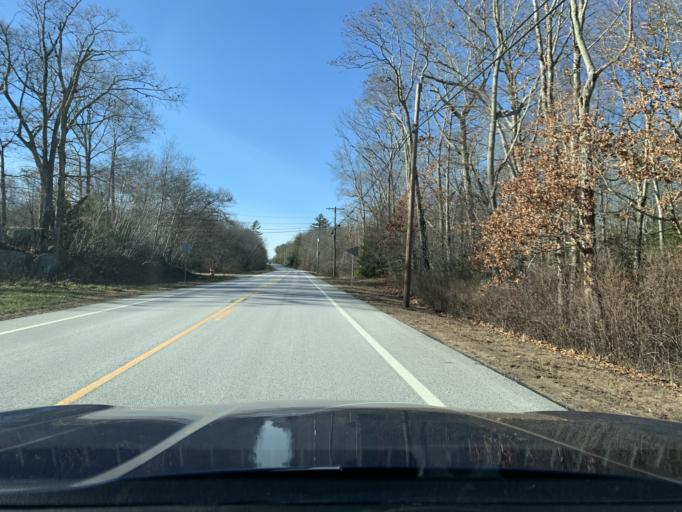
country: US
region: Rhode Island
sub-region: Washington County
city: Hope Valley
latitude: 41.5764
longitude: -71.7680
